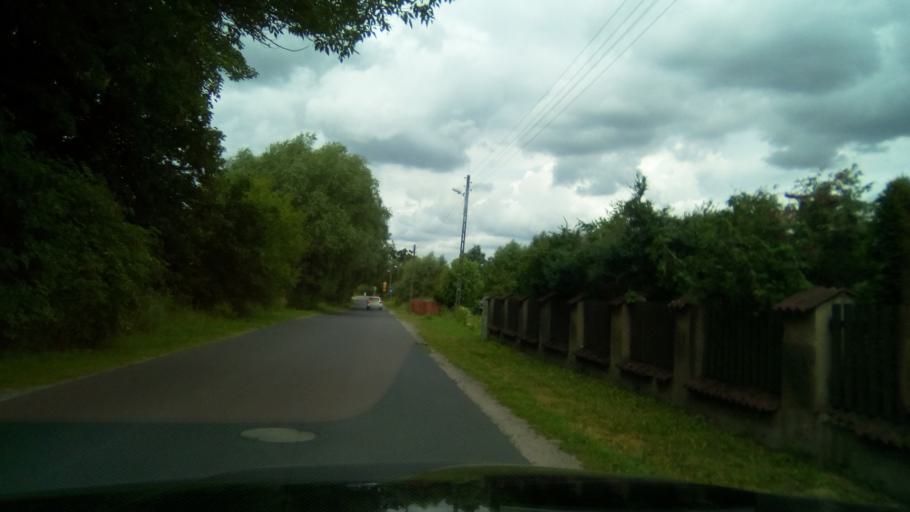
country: PL
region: Greater Poland Voivodeship
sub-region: Powiat gnieznienski
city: Gniezno
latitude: 52.5185
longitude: 17.6182
